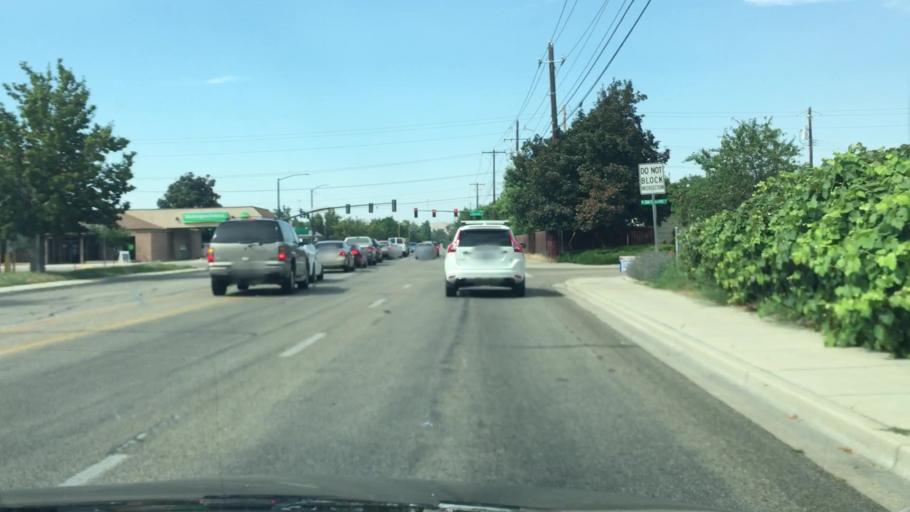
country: US
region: Idaho
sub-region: Ada County
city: Garden City
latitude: 43.6327
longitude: -116.2742
